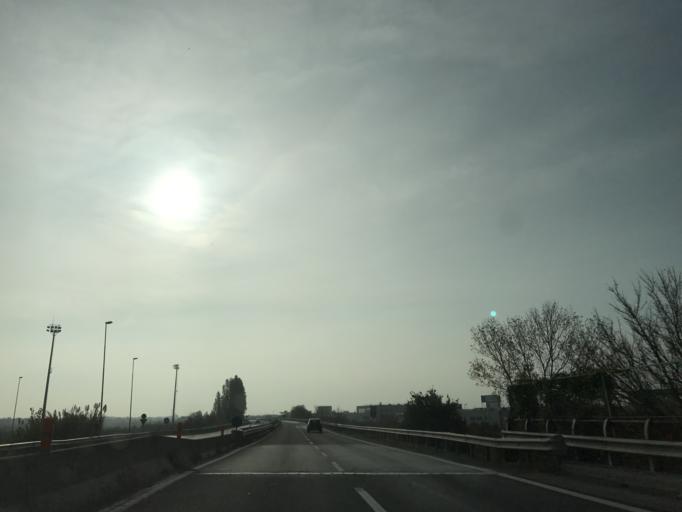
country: IT
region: Emilia-Romagna
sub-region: Forli-Cesena
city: Gatteo a Mare
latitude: 44.1656
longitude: 12.4267
